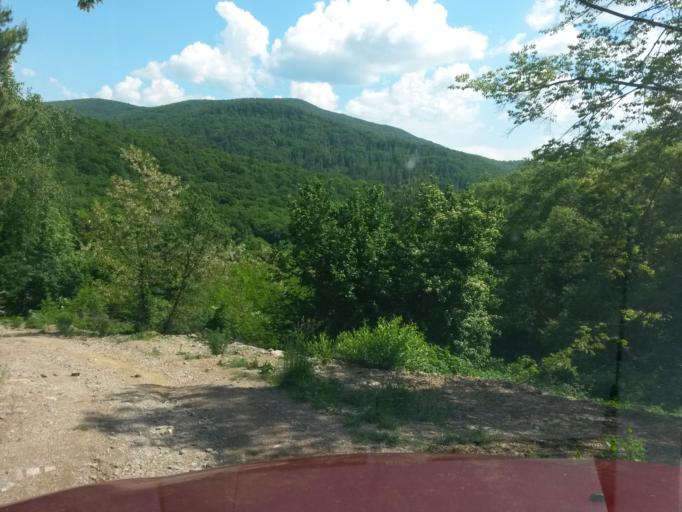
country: SK
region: Kosicky
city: Roznava
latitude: 48.6886
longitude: 20.5400
